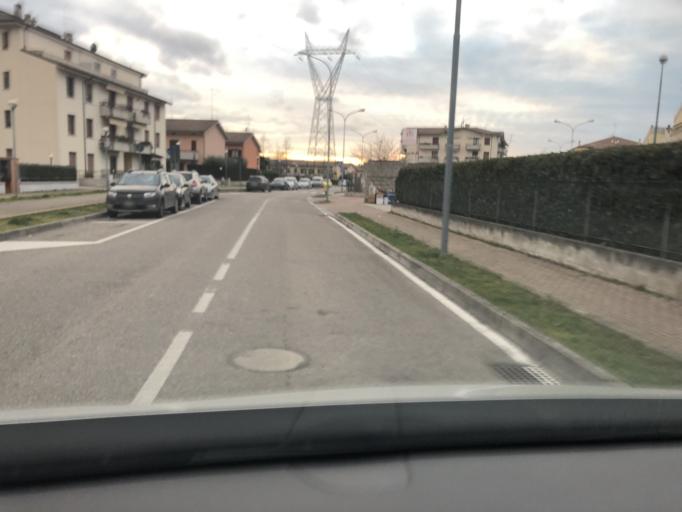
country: IT
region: Veneto
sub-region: Provincia di Verona
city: Bussolengo
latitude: 45.4630
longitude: 10.8543
